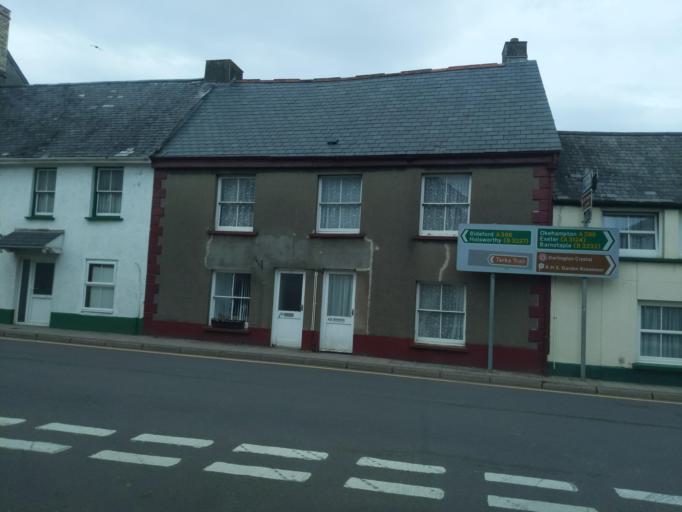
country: GB
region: England
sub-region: Devon
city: Great Torrington
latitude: 50.9526
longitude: -4.1458
